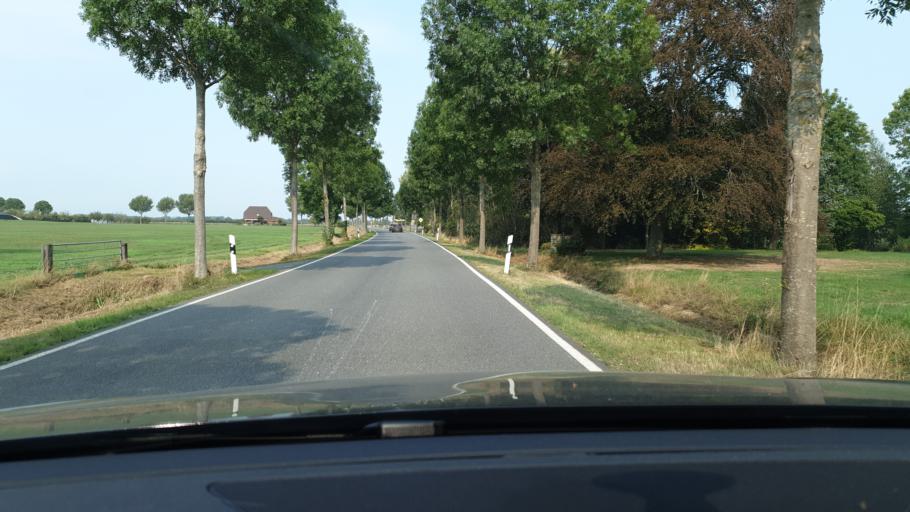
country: DE
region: North Rhine-Westphalia
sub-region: Regierungsbezirk Dusseldorf
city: Kranenburg
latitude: 51.8079
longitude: 6.0140
